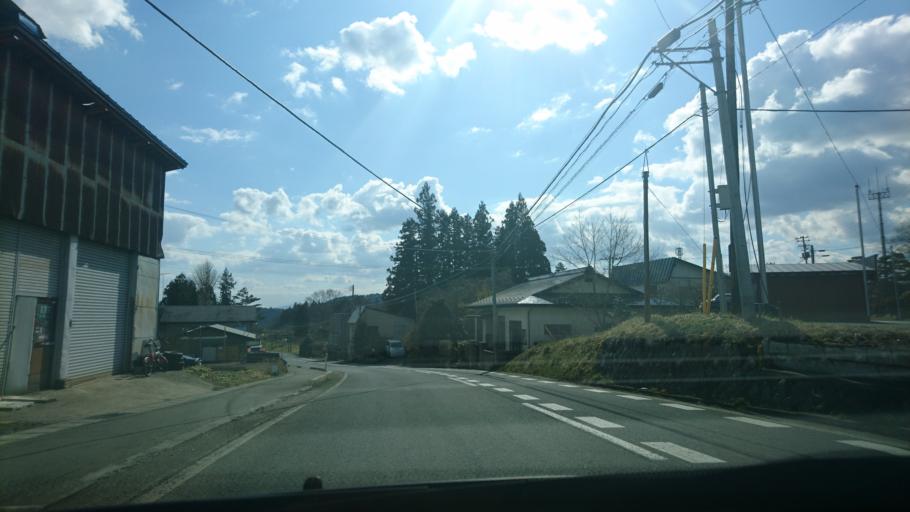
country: JP
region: Iwate
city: Kitakami
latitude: 39.2548
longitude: 141.2103
